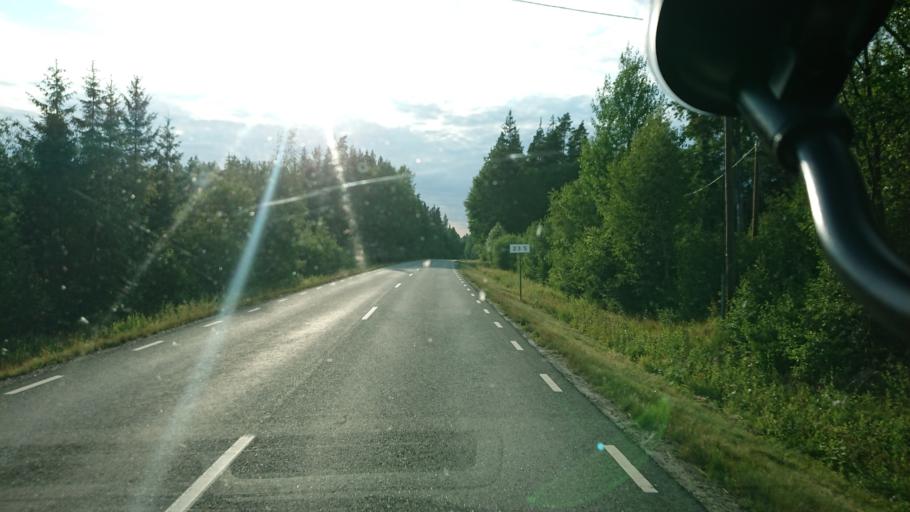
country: SE
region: Kronoberg
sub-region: Vaxjo Kommun
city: Rottne
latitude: 57.0351
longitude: 14.9268
